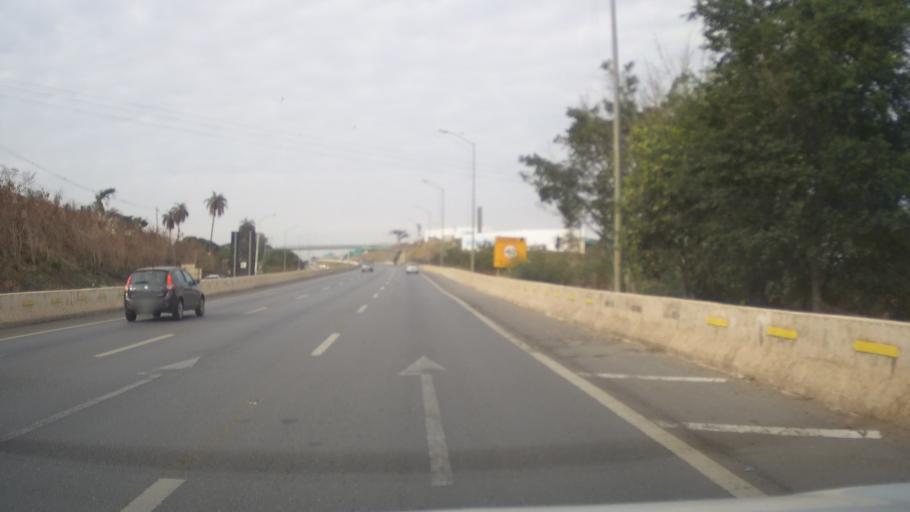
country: BR
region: Minas Gerais
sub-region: Vespasiano
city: Vespasiano
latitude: -19.7314
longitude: -43.9426
